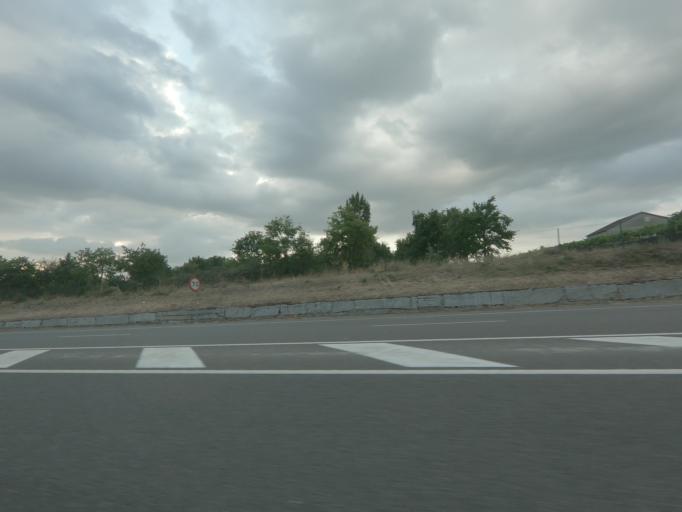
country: ES
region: Galicia
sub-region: Provincia de Ourense
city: Taboadela
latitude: 42.2856
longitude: -7.8340
